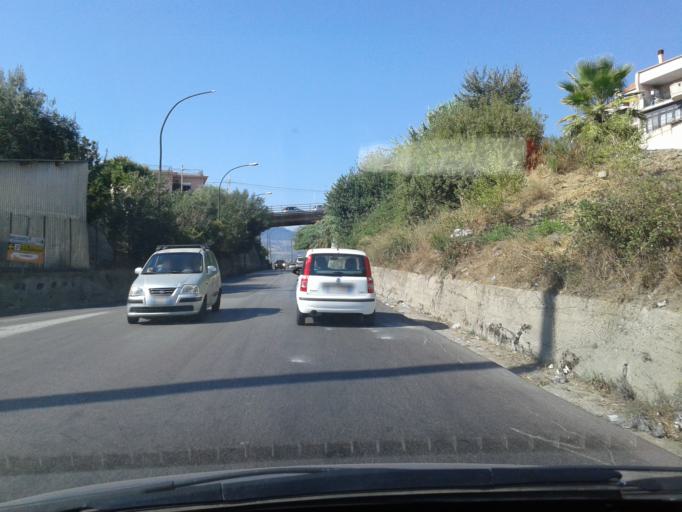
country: IT
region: Sicily
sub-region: Palermo
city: Monreale
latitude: 38.0758
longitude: 13.2879
